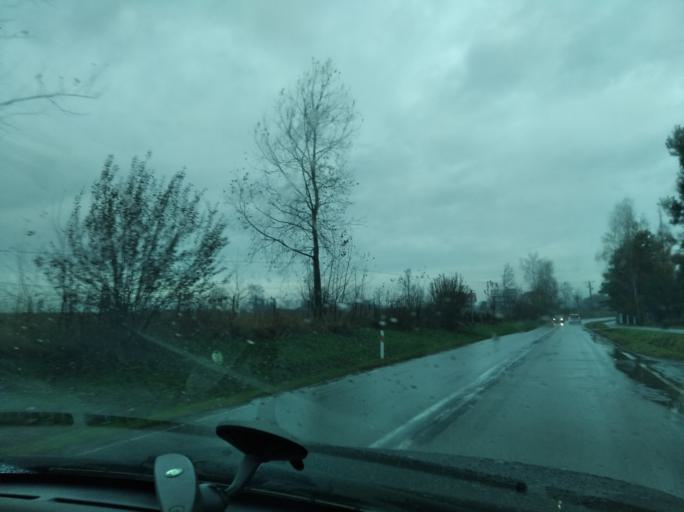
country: PL
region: Subcarpathian Voivodeship
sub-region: Powiat lancucki
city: Albigowa
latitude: 50.0326
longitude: 22.2285
